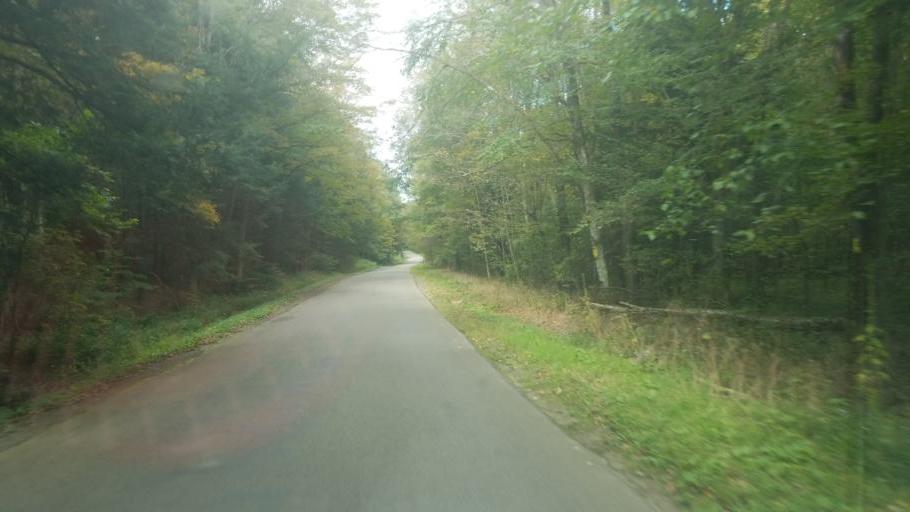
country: US
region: New York
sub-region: Cattaraugus County
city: Weston Mills
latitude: 42.1485
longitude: -78.3546
